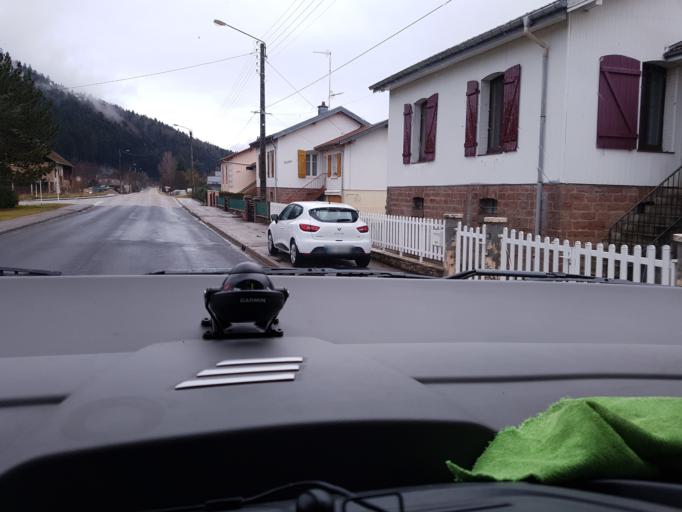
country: FR
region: Lorraine
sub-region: Departement des Vosges
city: Saint-Die-des-Vosges
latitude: 48.2907
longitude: 6.9235
